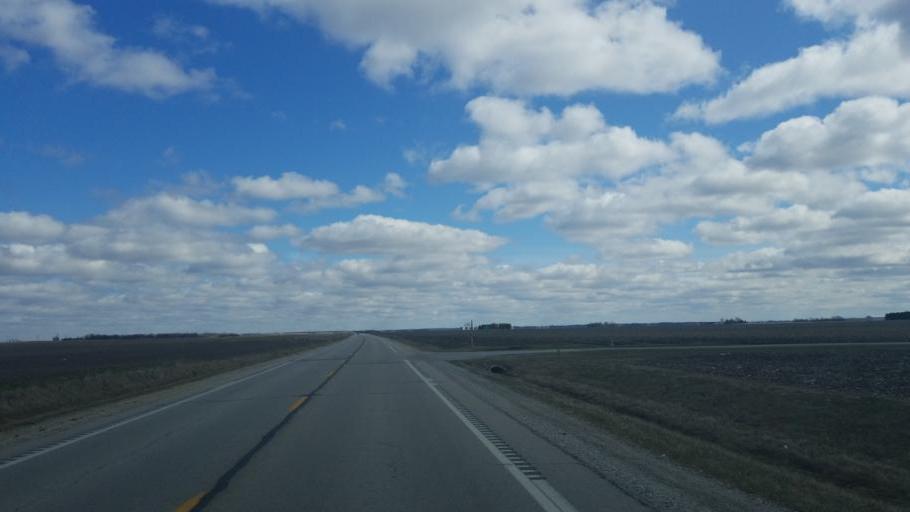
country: US
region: Illinois
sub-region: Douglas County
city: Villa Grove
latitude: 39.7919
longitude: -88.1206
